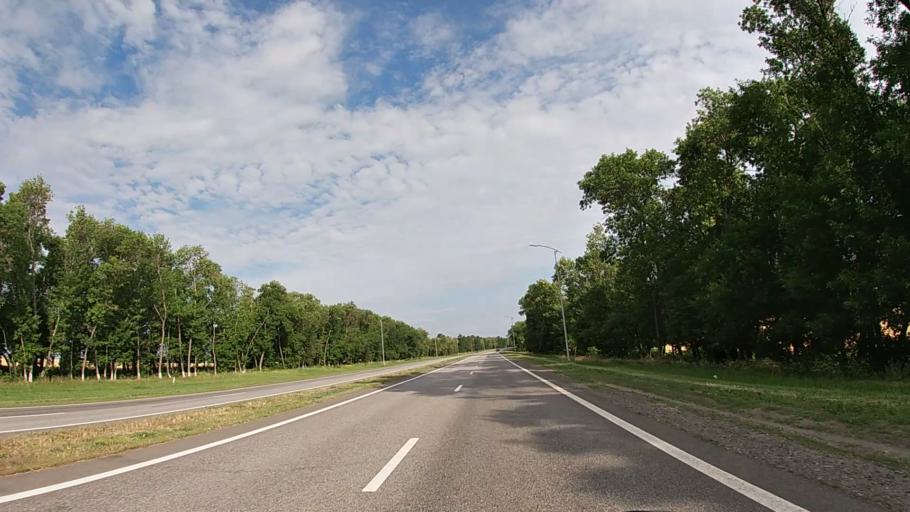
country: RU
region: Belgorod
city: Tomarovka
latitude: 50.6712
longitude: 36.3015
